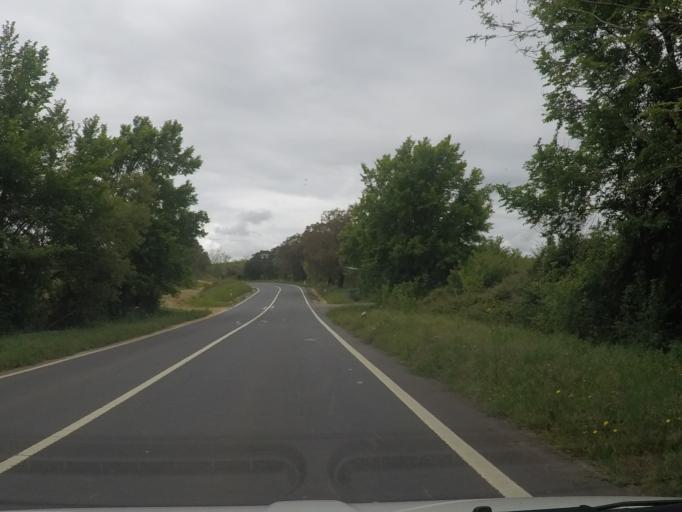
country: PT
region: Setubal
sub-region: Santiago do Cacem
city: Cercal
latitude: 37.8277
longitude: -8.6975
